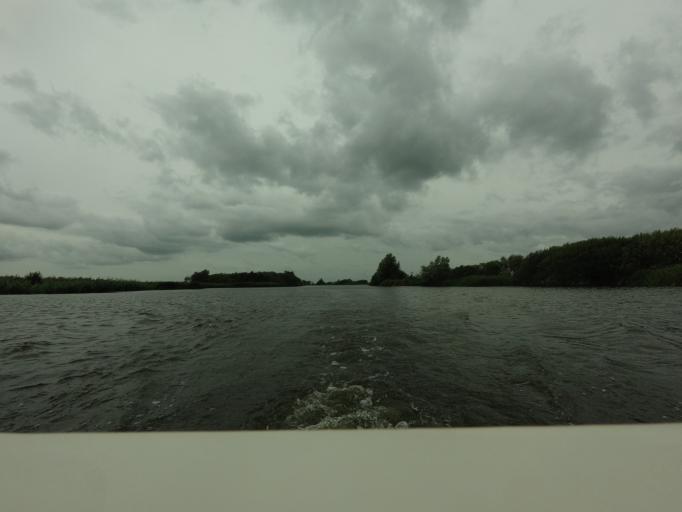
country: NL
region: Friesland
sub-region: Gemeente Boarnsterhim
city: Warten
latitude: 53.1006
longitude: 5.9145
